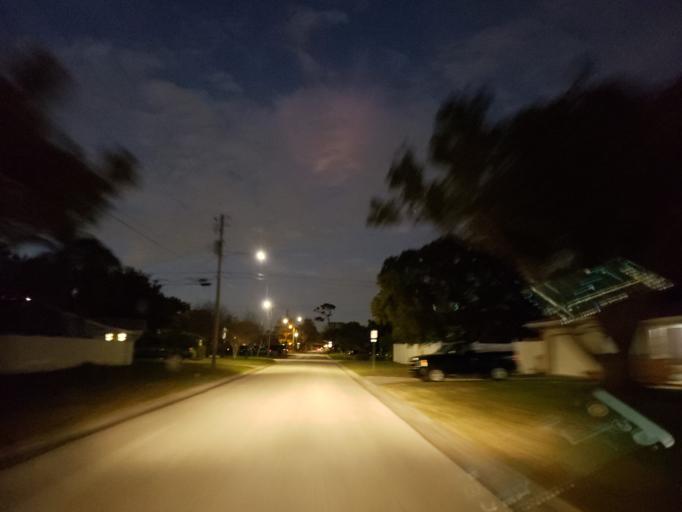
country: US
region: Florida
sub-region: Pinellas County
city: West and East Lealman
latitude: 27.8050
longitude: -82.6939
